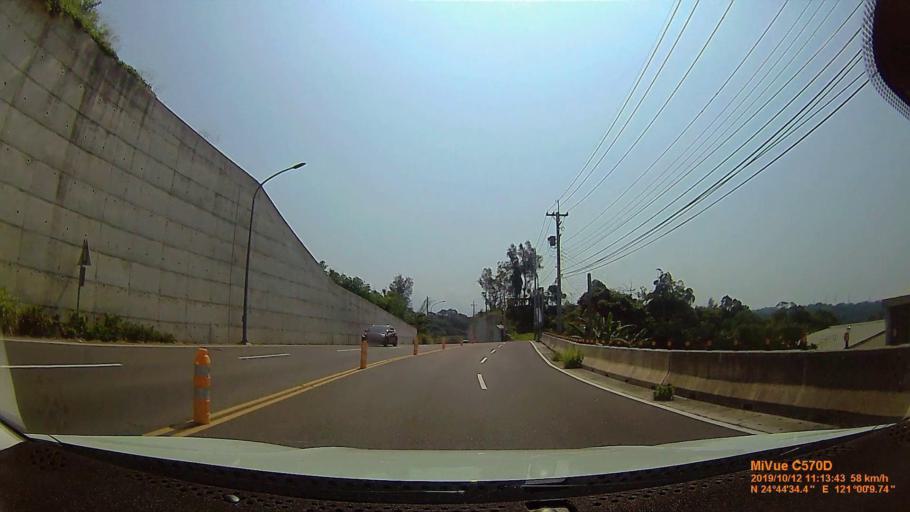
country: TW
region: Taiwan
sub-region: Hsinchu
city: Hsinchu
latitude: 24.7428
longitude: 121.0028
